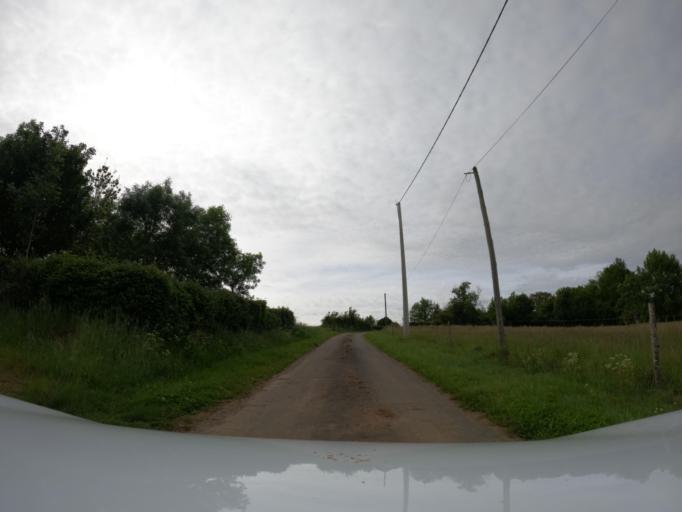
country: FR
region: Pays de la Loire
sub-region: Departement de la Vendee
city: Saint-Hilaire-des-Loges
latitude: 46.4817
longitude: -0.6641
